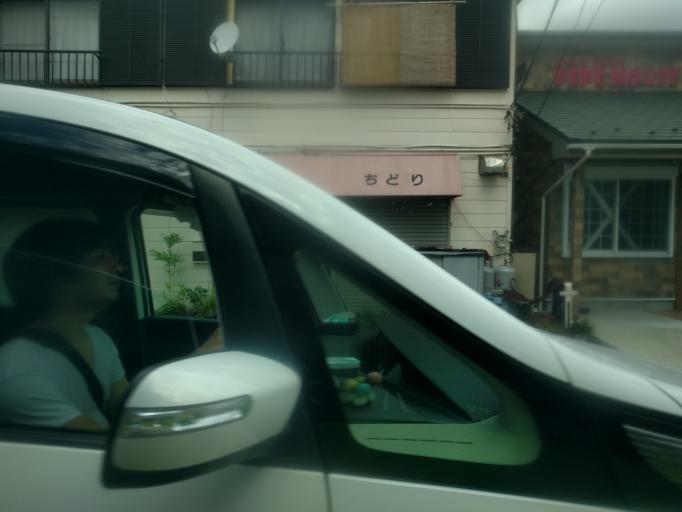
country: JP
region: Saitama
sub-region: Kawaguchi-shi
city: Hatogaya-honcho
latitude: 35.8243
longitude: 139.7296
